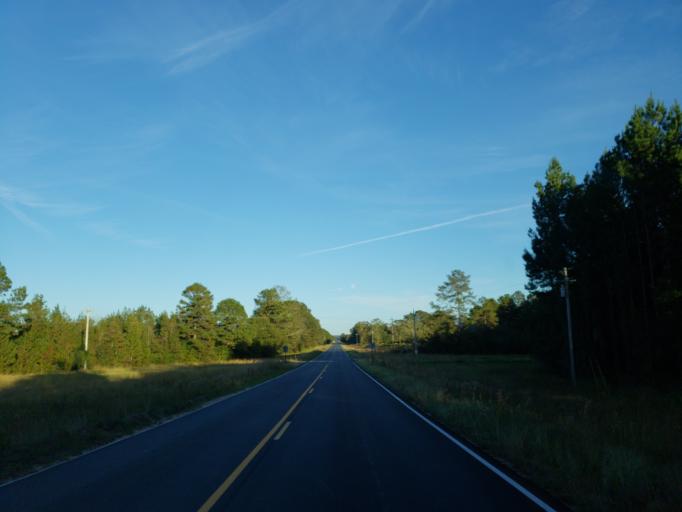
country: US
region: Mississippi
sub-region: Wayne County
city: Belmont
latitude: 31.4258
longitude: -88.5624
